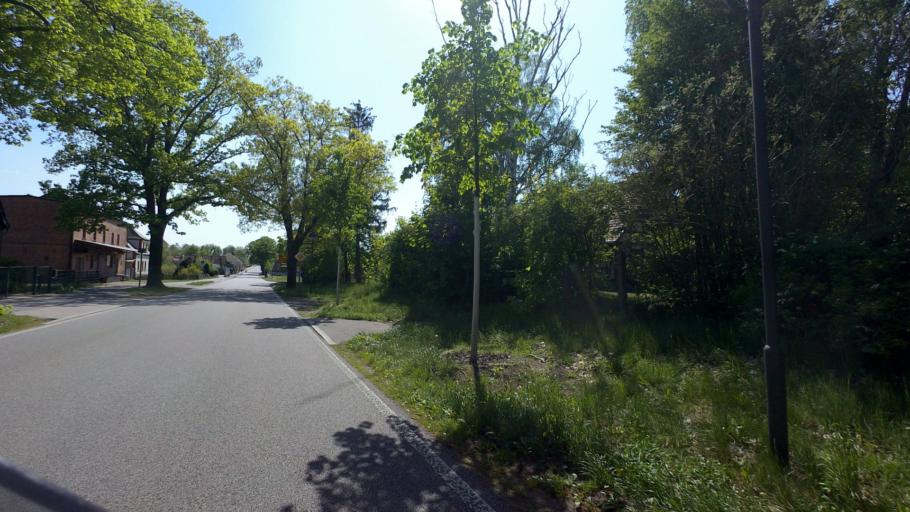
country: DE
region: Brandenburg
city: Tauche
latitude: 52.0884
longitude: 14.1720
